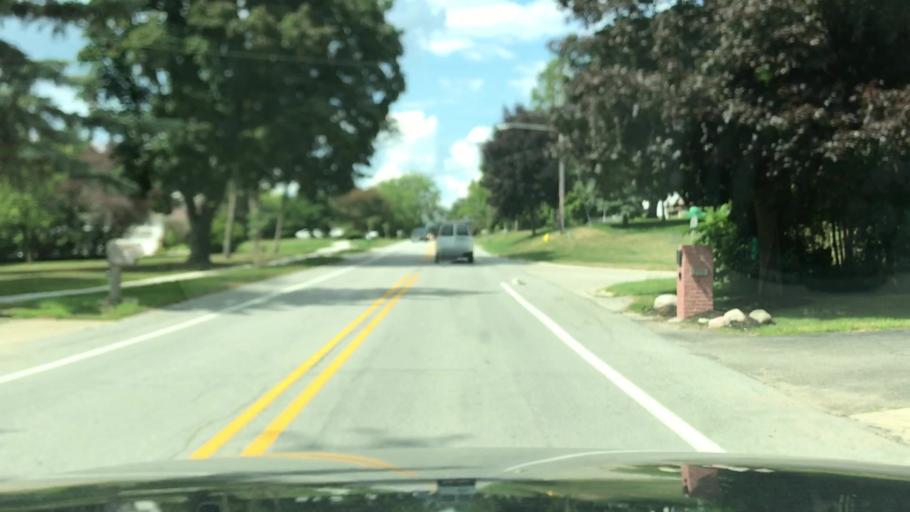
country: US
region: Michigan
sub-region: Kent County
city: East Grand Rapids
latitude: 42.9803
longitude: -85.6104
